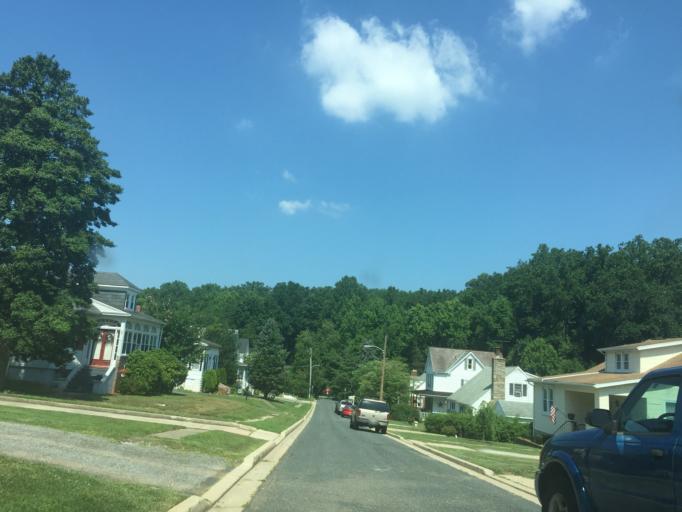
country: US
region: Maryland
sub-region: Baltimore County
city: Overlea
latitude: 39.3640
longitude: -76.5248
